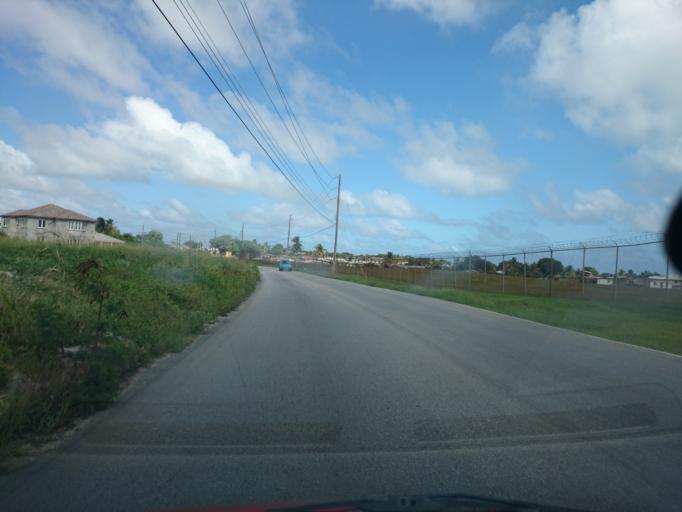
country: BB
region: Saint Philip
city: Crane
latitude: 13.0842
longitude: -59.4801
